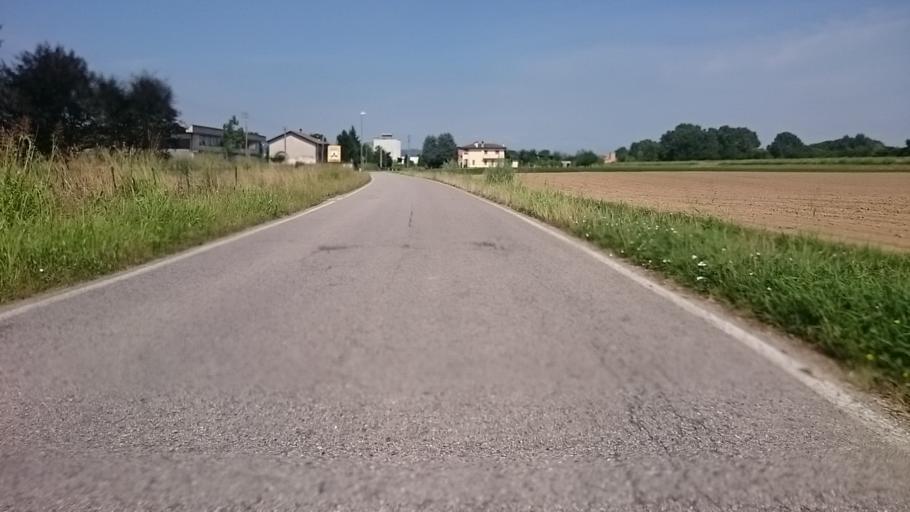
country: IT
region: Veneto
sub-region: Provincia di Padova
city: Cervarese Santa Croce
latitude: 45.4211
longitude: 11.7000
